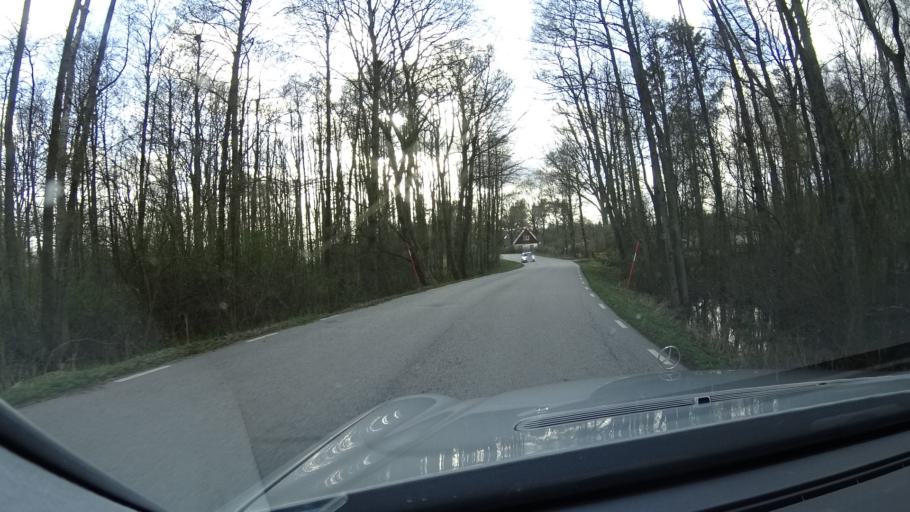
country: SE
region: Skane
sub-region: Hoors Kommun
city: Satofta
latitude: 55.9031
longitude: 13.5944
